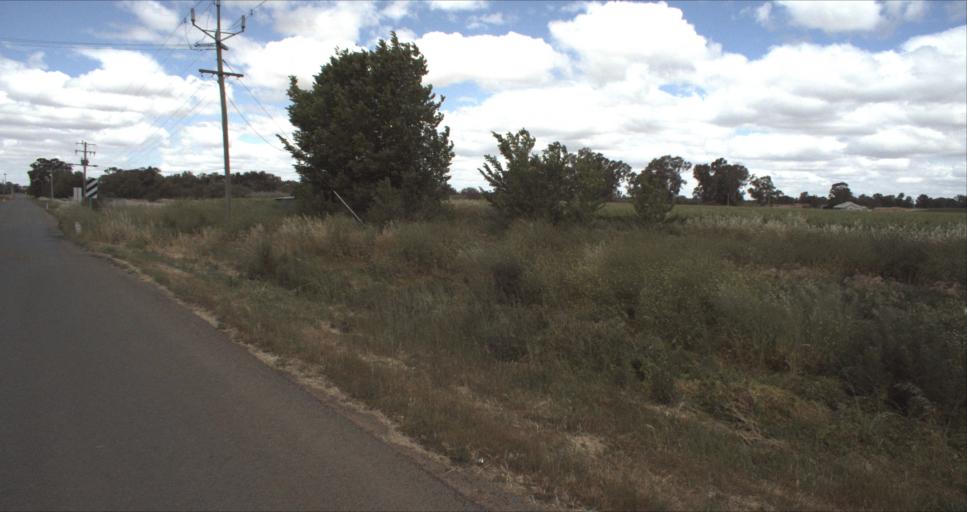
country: AU
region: New South Wales
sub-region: Leeton
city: Leeton
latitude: -34.5898
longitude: 146.3956
